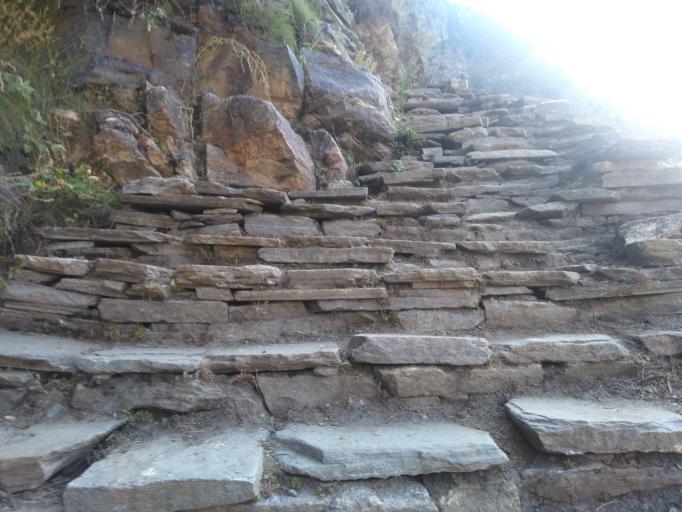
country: NP
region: Western Region
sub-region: Dhawalagiri Zone
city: Jomsom
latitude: 28.9041
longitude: 83.0295
